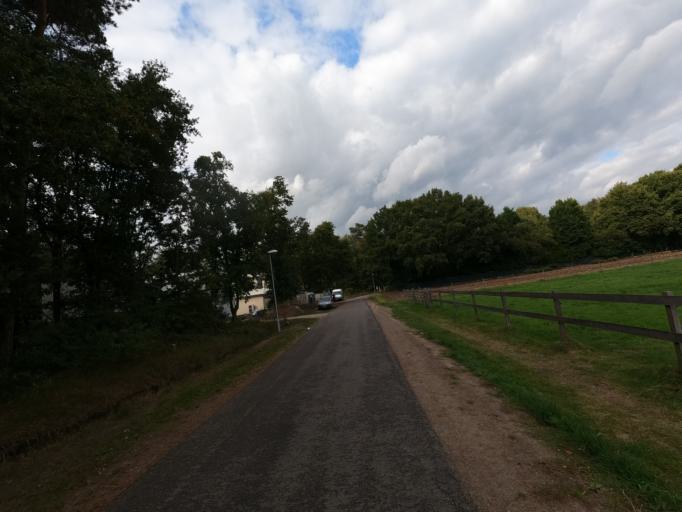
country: BE
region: Flanders
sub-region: Provincie Antwerpen
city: Kasterlee
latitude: 51.2091
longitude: 4.9133
